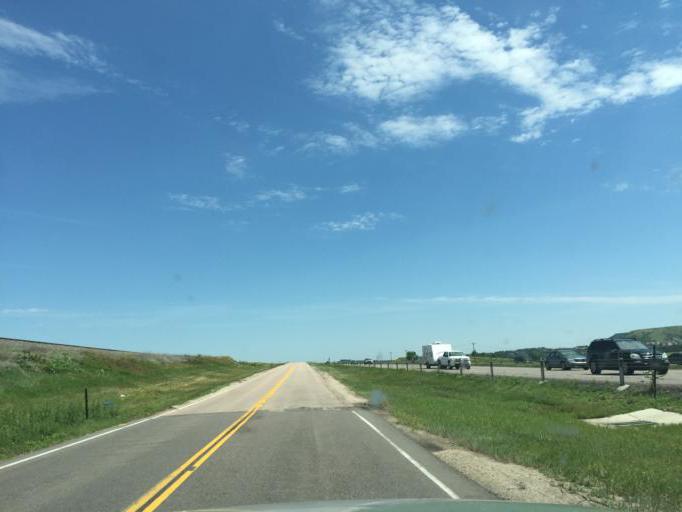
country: US
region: Colorado
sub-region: Douglas County
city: Castle Rock
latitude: 39.3209
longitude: -104.8828
